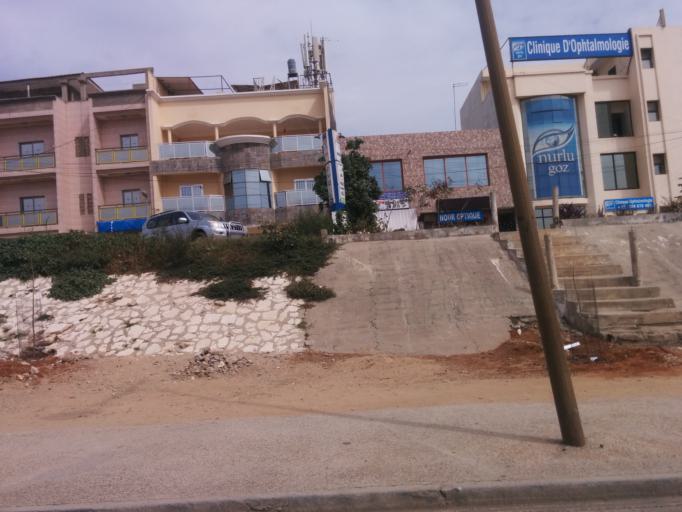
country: SN
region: Dakar
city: Mermoz Boabab
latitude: 14.7336
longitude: -17.4732
